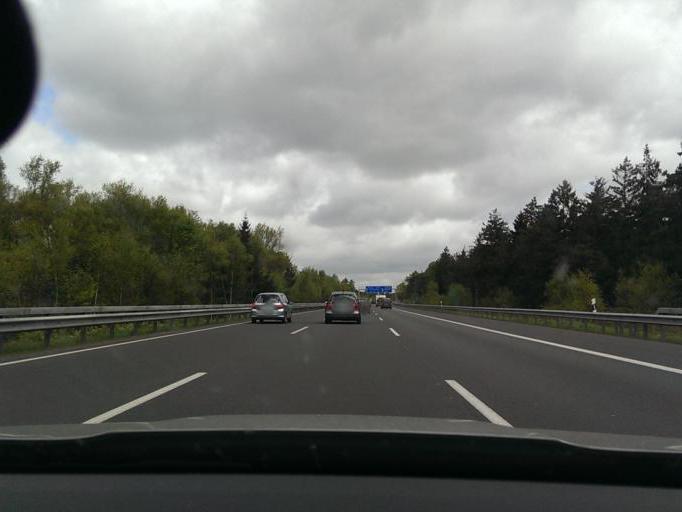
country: DE
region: Lower Saxony
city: Hademstorf
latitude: 52.7584
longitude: 9.6655
